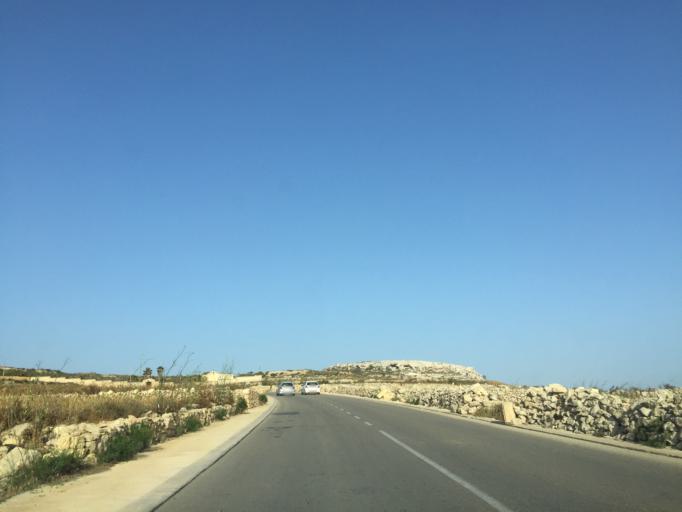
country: MT
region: Saint Lawrence
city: San Lawrenz
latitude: 36.0504
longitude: 14.1976
